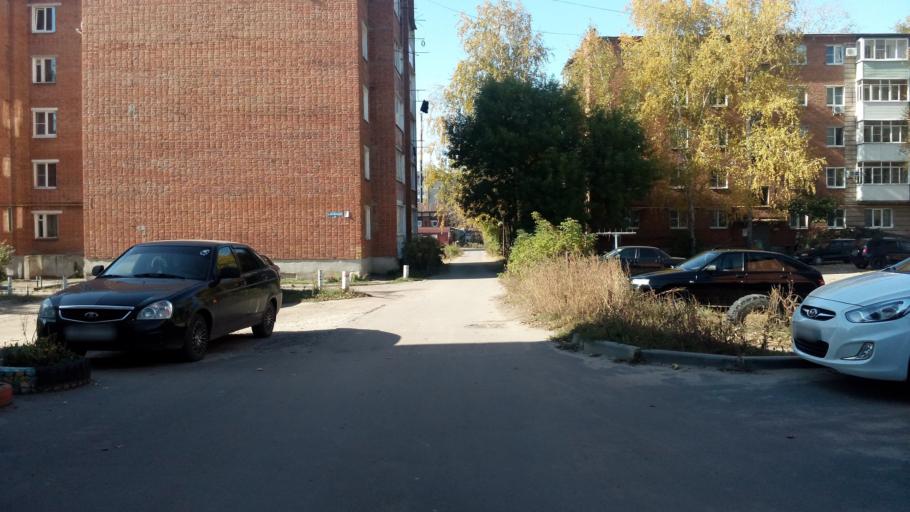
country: RU
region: Tambov
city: Kotovsk
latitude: 52.5838
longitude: 41.4998
